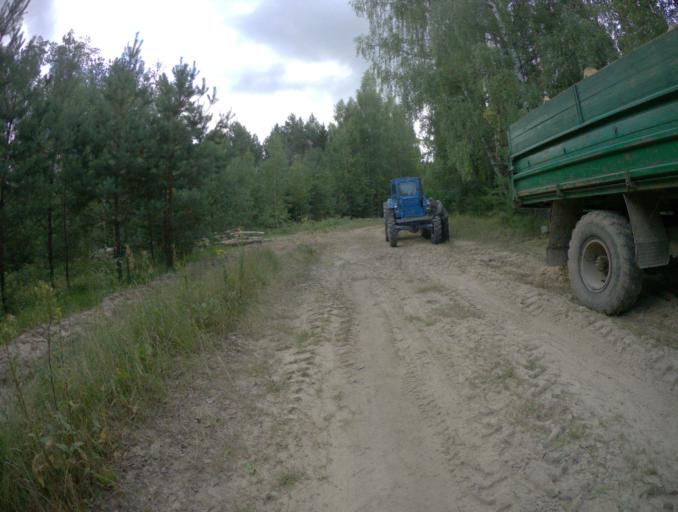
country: RU
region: Vladimir
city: Vorsha
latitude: 55.9460
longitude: 40.1451
